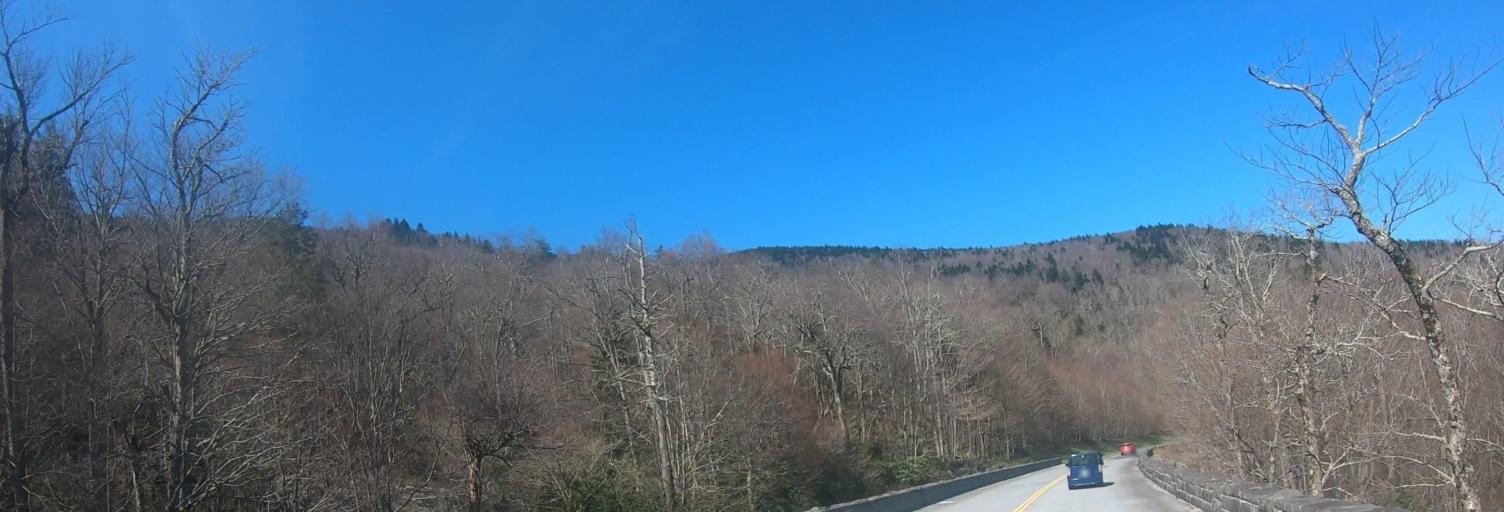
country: US
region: North Carolina
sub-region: Watauga County
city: Foscoe
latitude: 36.1000
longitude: -81.8106
